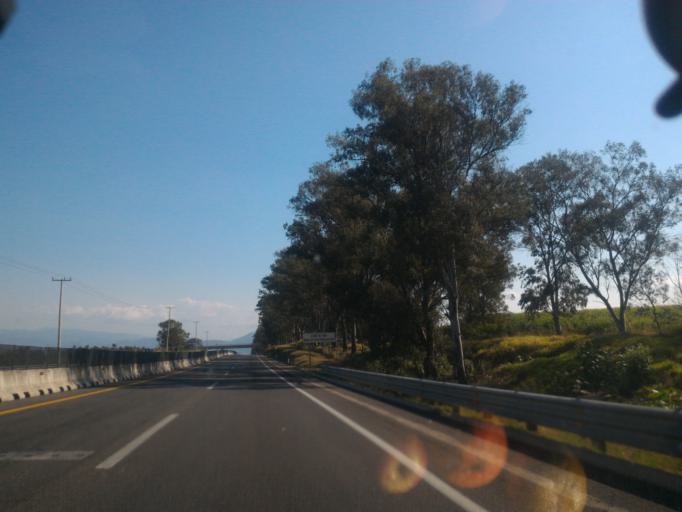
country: MX
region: Jalisco
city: Zapotiltic
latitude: 19.5988
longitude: -103.4544
